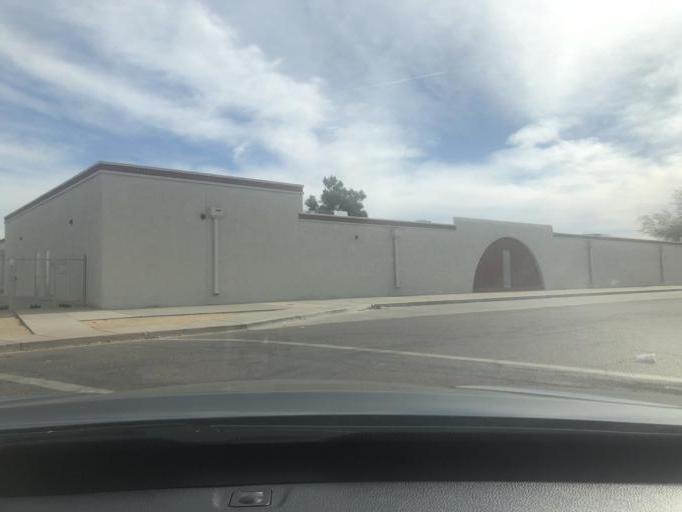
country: US
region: Arizona
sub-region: Maricopa County
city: Phoenix
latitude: 33.4578
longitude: -112.0456
